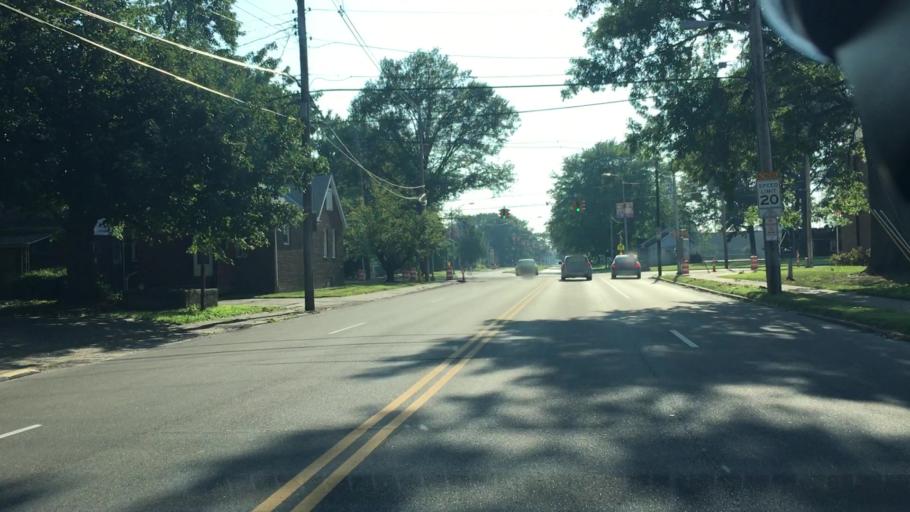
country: US
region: Indiana
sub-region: Vanderburgh County
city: Evansville
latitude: 37.9736
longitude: -87.5286
